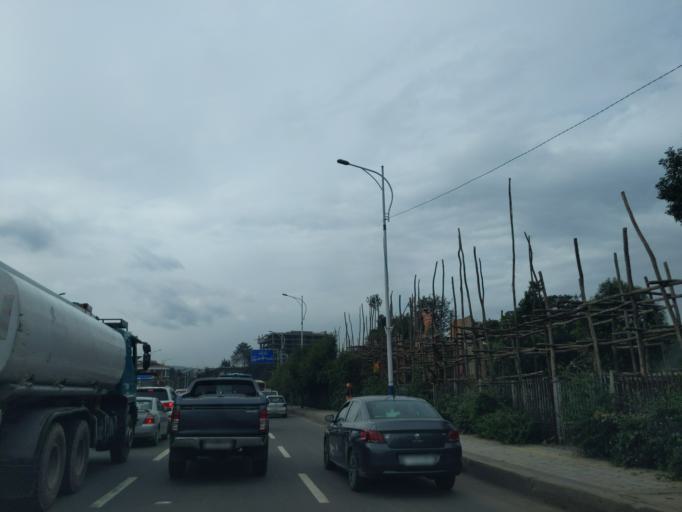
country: ET
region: Adis Abeba
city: Addis Ababa
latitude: 9.0281
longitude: 38.7633
